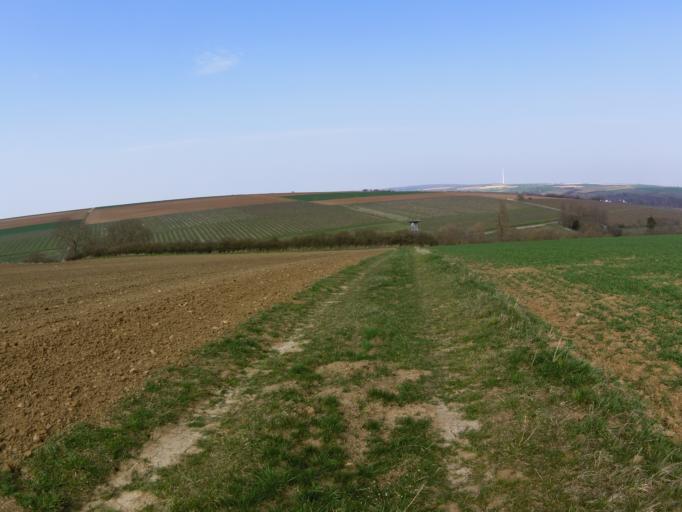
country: DE
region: Bavaria
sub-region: Regierungsbezirk Unterfranken
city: Mainstockheim
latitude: 49.7921
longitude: 10.1455
